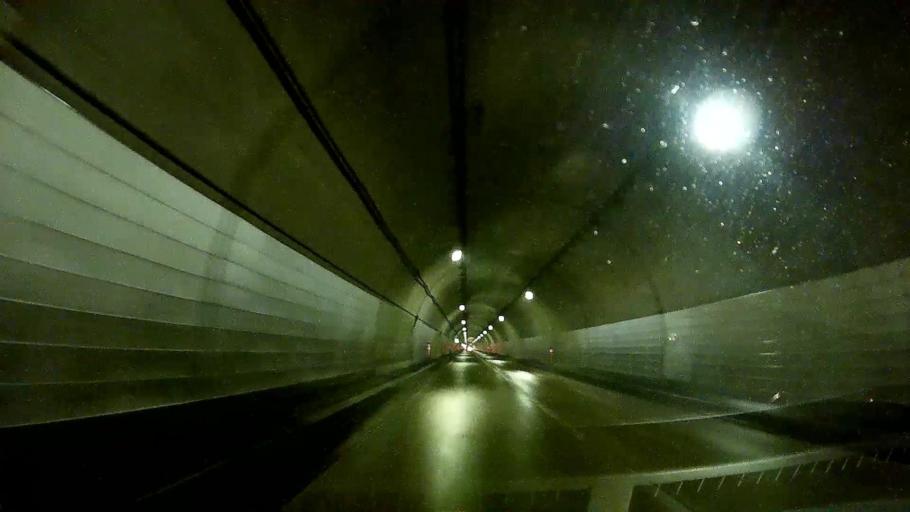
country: JP
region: Niigata
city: Shiozawa
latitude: 37.0300
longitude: 138.7906
